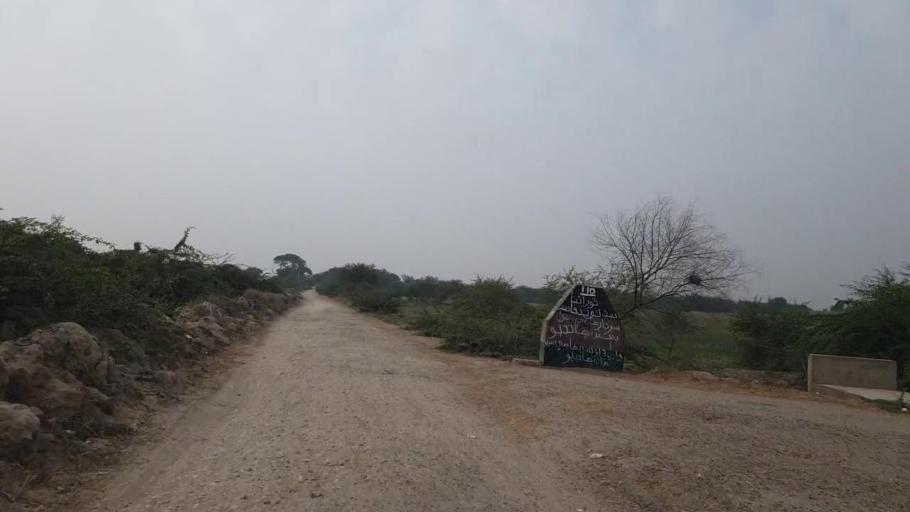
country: PK
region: Sindh
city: Kario
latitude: 24.9112
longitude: 68.5382
